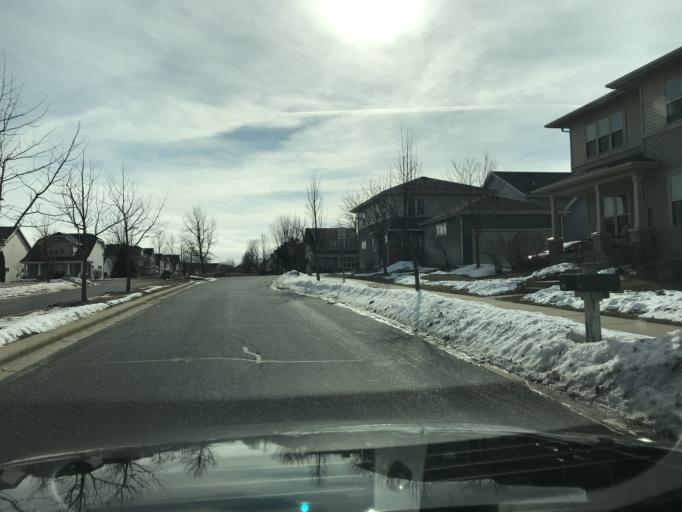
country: US
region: Wisconsin
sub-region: Dane County
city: Monona
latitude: 43.0894
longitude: -89.2782
